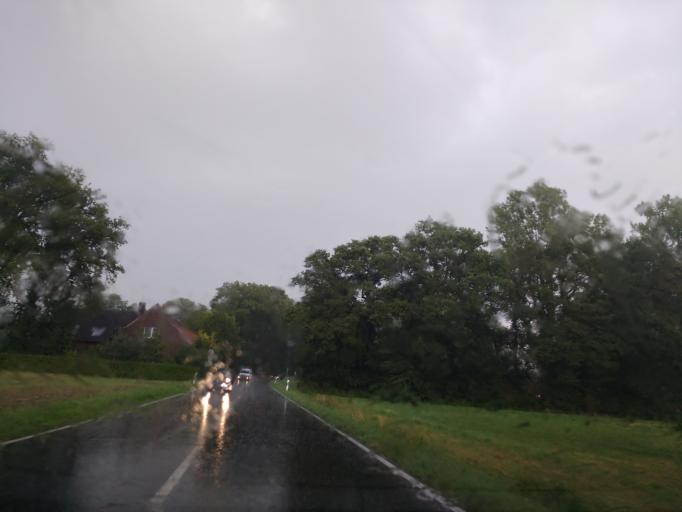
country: DE
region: North Rhine-Westphalia
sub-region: Regierungsbezirk Munster
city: Lienen
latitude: 52.1143
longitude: 7.9333
